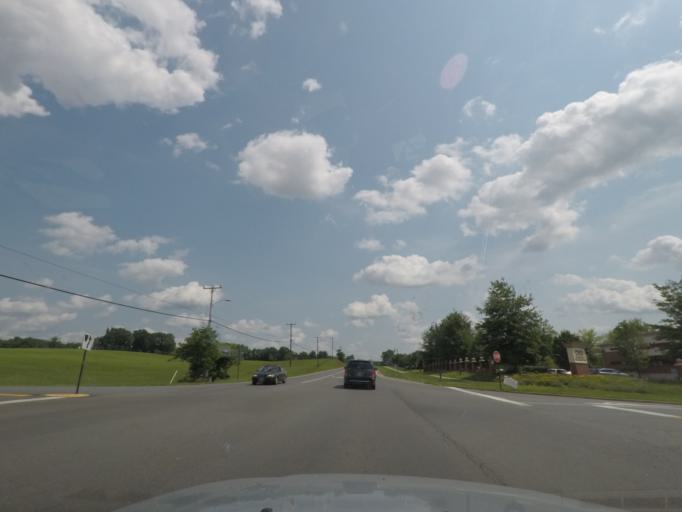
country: US
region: Virginia
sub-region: Orange County
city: Orange
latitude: 38.2610
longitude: -78.1173
